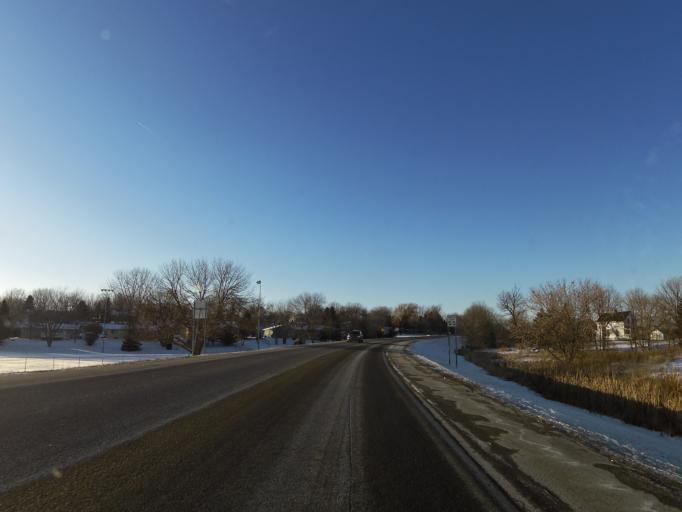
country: US
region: Minnesota
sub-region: Rice County
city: Lonsdale
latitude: 44.4811
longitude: -93.4347
